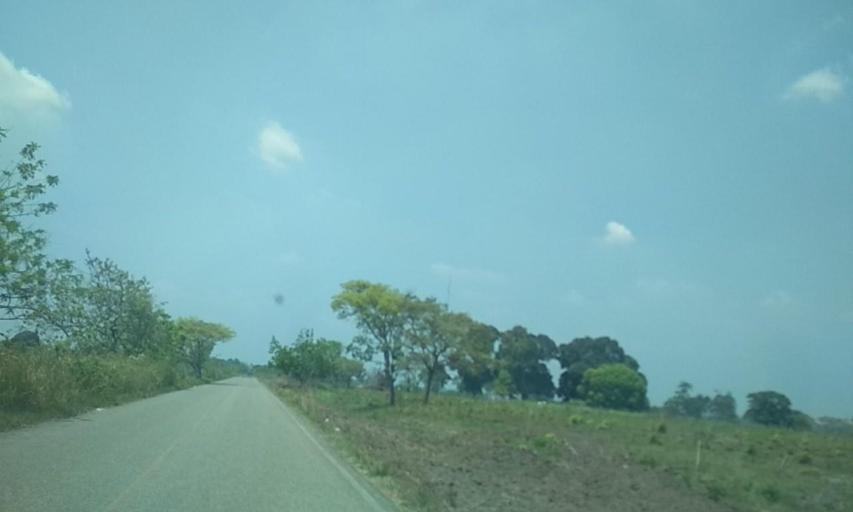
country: MX
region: Tabasco
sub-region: Huimanguillo
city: Paso de la Mina 3ra. Seccion
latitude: 17.8357
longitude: -93.6160
